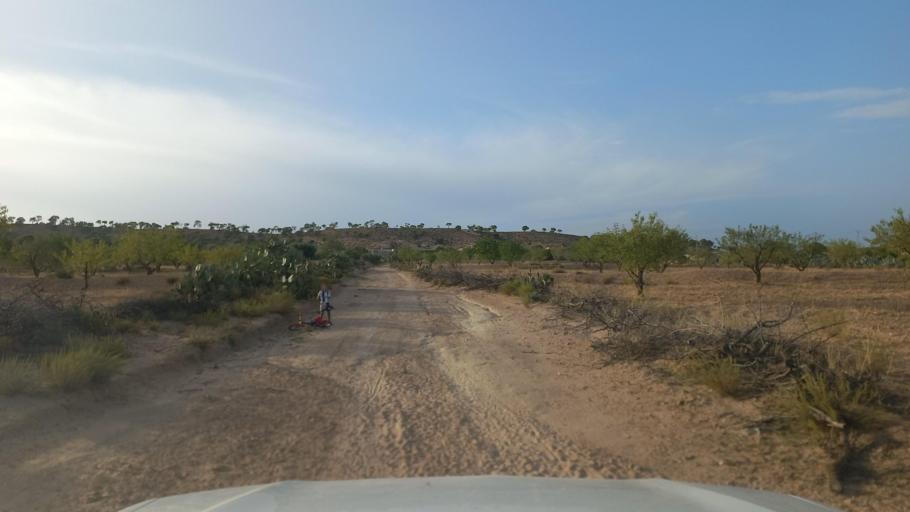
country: TN
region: Al Qasrayn
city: Sbiba
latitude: 35.4038
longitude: 8.8988
